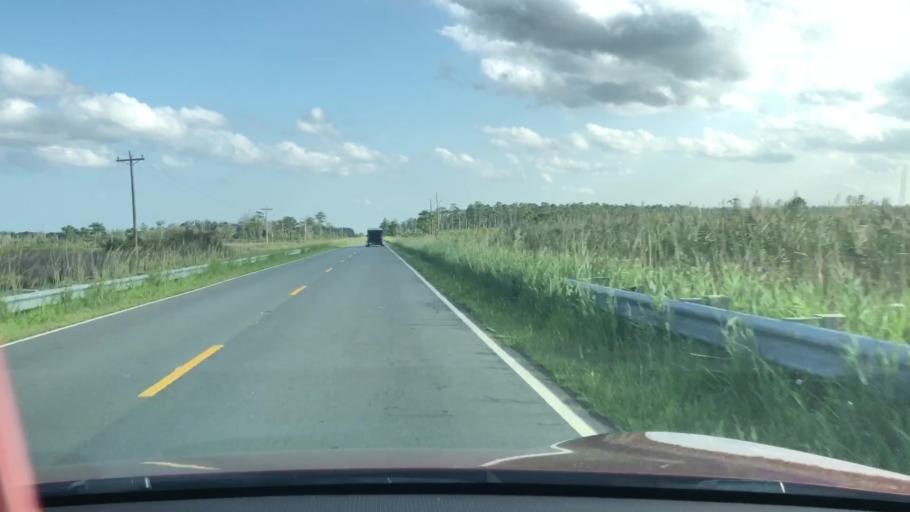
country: US
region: North Carolina
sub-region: Dare County
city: Wanchese
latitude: 35.6861
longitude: -75.7806
